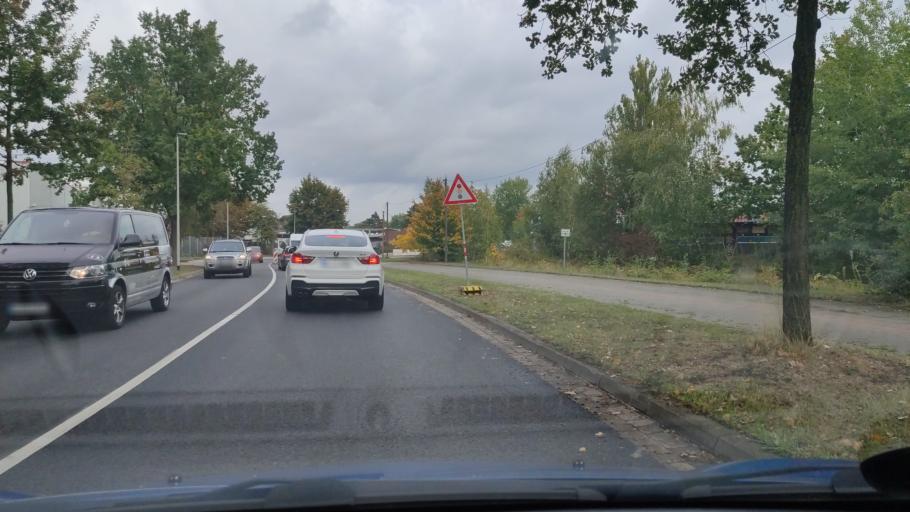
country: DE
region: Lower Saxony
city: Hannover
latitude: 52.3727
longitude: 9.6829
